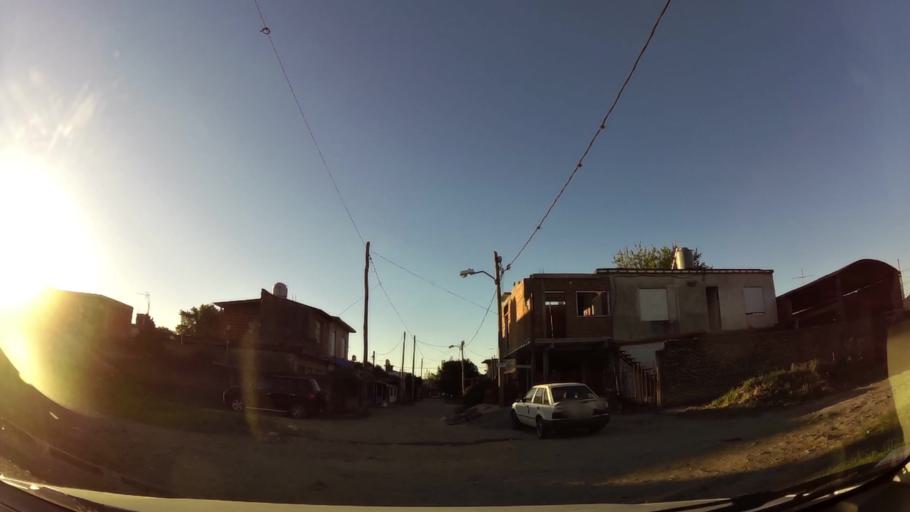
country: AR
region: Buenos Aires
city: San Justo
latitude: -34.7238
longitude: -58.6124
